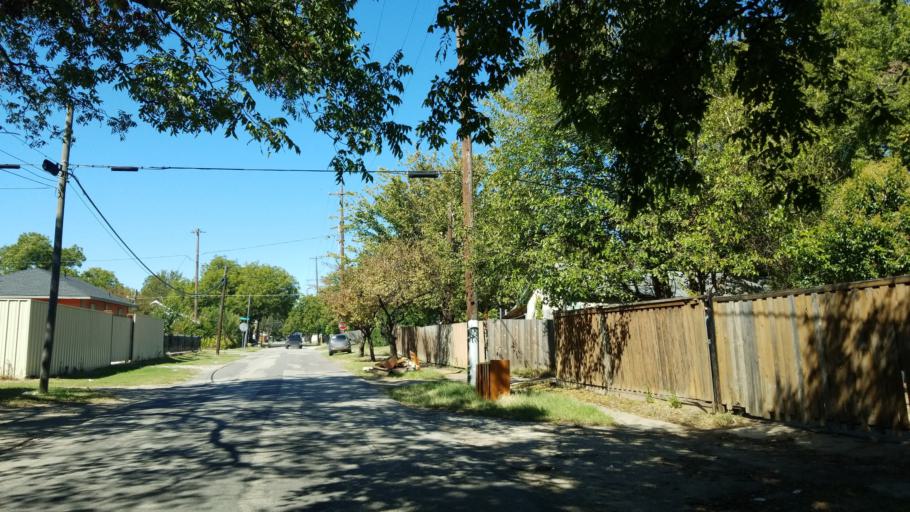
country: US
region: Texas
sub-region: Dallas County
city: Dallas
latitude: 32.7922
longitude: -96.7548
